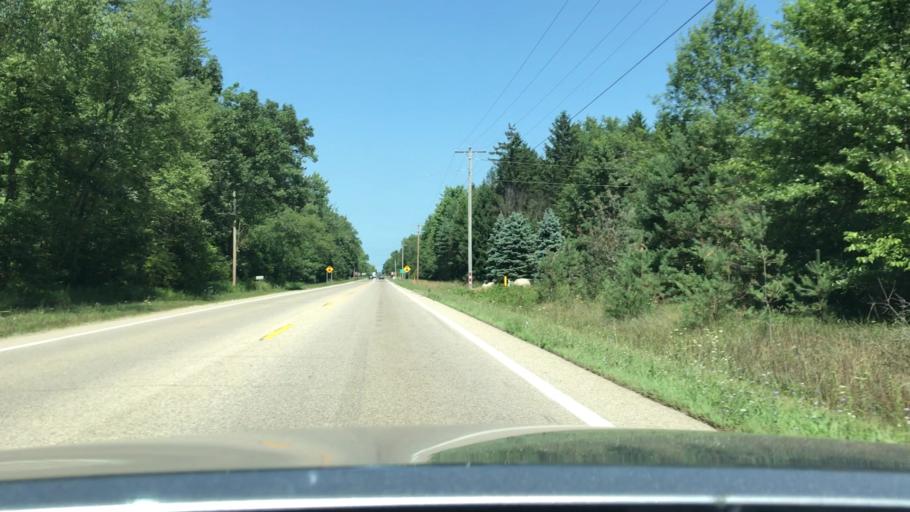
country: US
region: Michigan
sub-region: Ottawa County
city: Allendale
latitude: 42.9396
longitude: -86.0819
